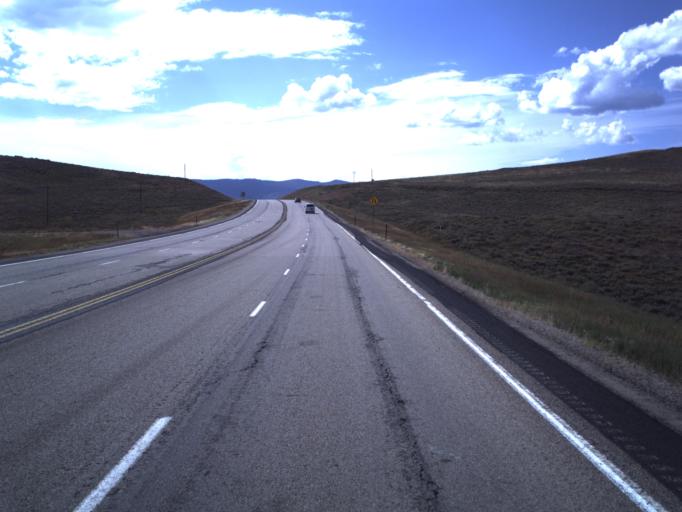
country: US
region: Utah
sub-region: Wasatch County
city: Heber
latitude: 40.1950
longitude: -111.0907
